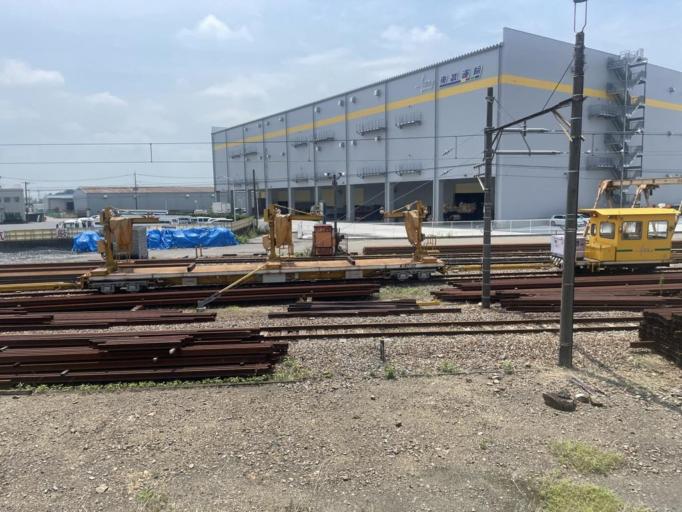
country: JP
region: Gunma
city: Tatebayashi
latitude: 36.2661
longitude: 139.5495
